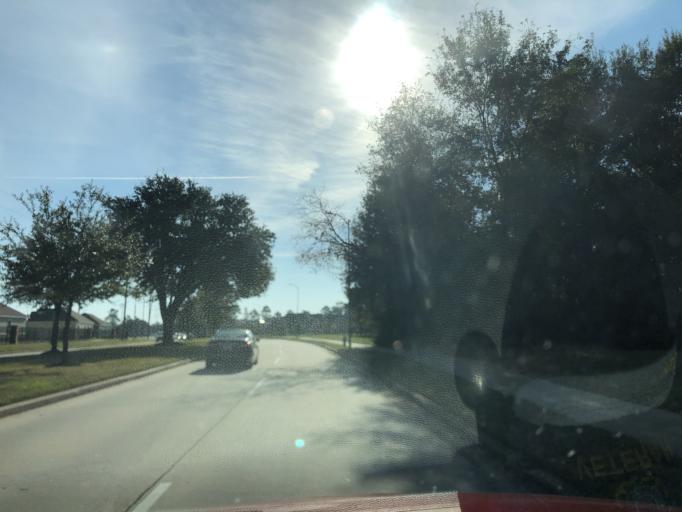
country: US
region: Texas
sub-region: Harris County
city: Tomball
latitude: 30.0354
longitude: -95.5596
